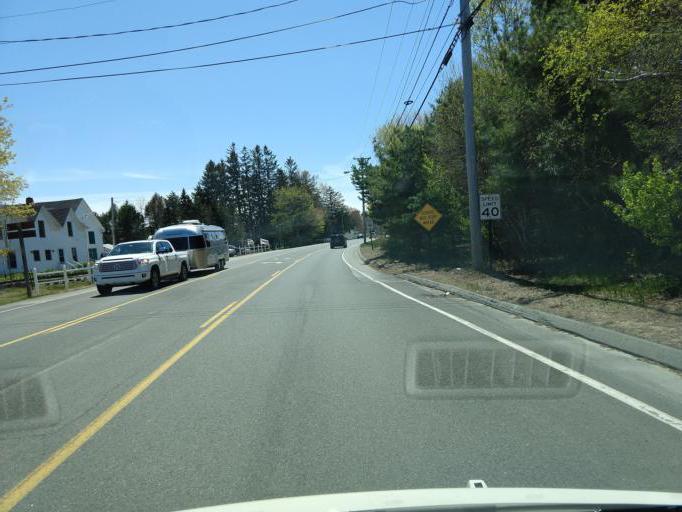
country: US
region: Maine
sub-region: York County
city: Wells Beach Station
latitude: 43.2907
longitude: -70.5908
